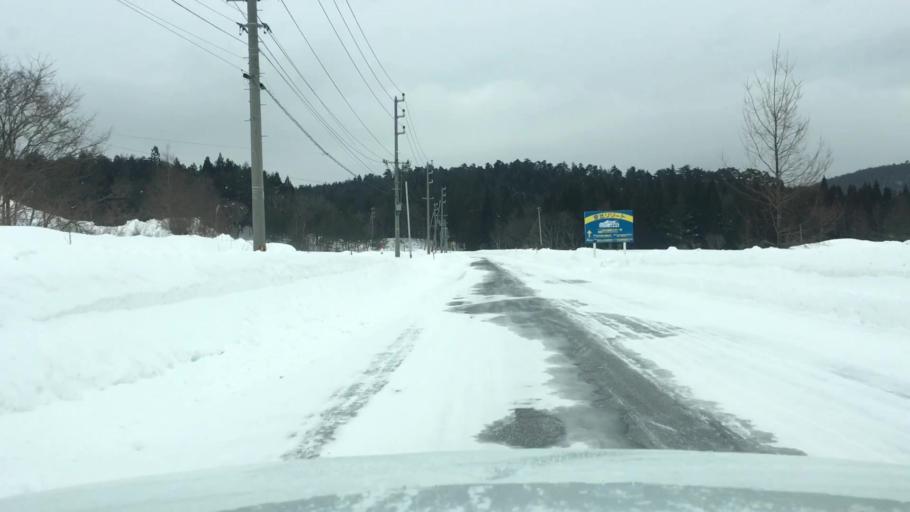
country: JP
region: Akita
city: Hanawa
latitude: 39.9925
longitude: 140.9957
